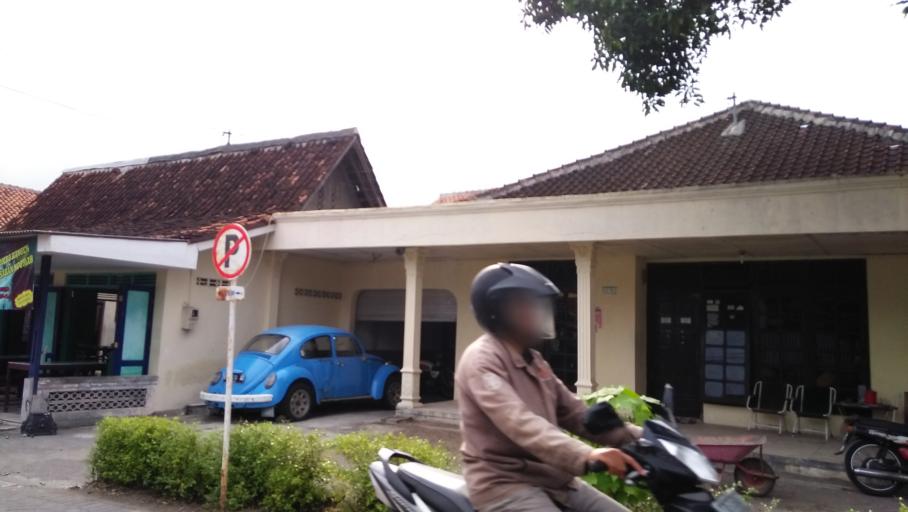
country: ID
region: Daerah Istimewa Yogyakarta
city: Yogyakarta
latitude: -7.7650
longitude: 110.3870
